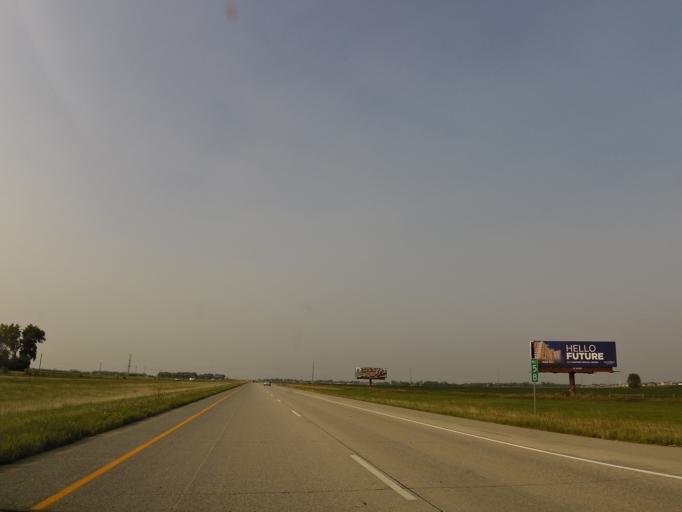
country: US
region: North Dakota
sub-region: Cass County
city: Horace
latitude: 46.7710
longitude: -96.8392
